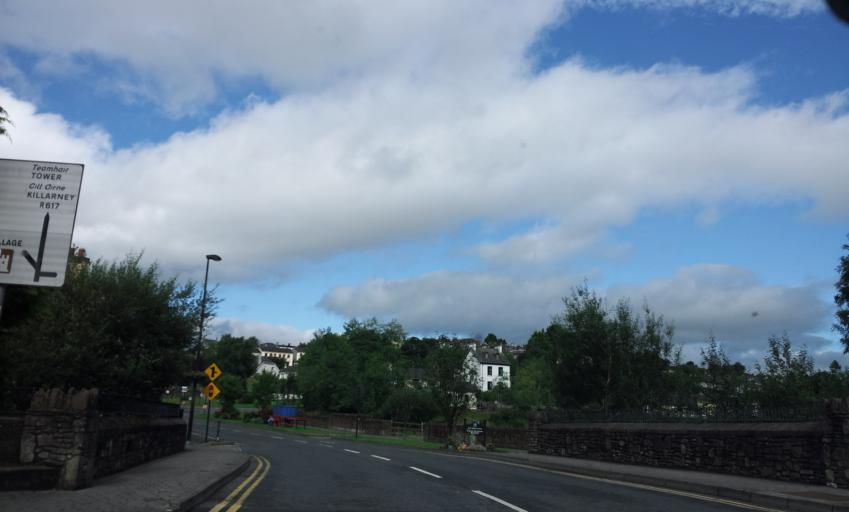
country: IE
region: Munster
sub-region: County Cork
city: Blarney
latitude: 51.9337
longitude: -8.5612
